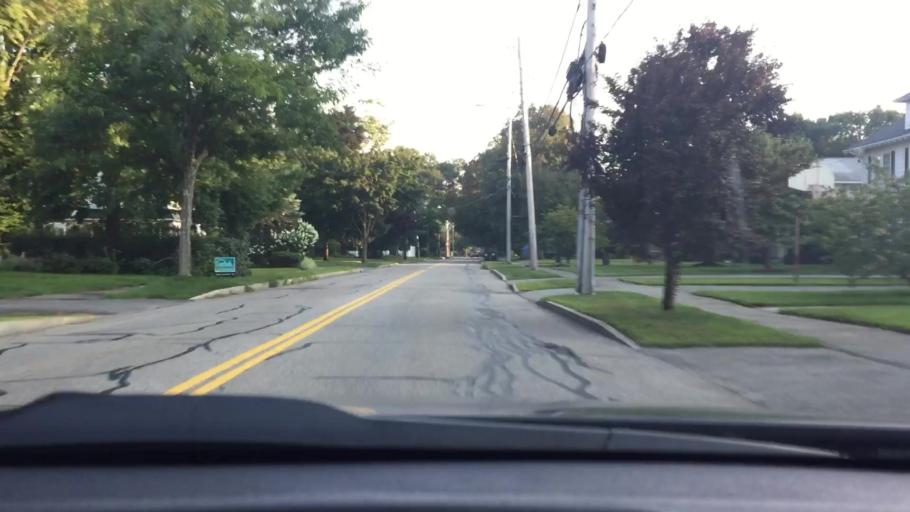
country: US
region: Massachusetts
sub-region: Norfolk County
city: Needham
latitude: 42.2800
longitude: -71.2299
